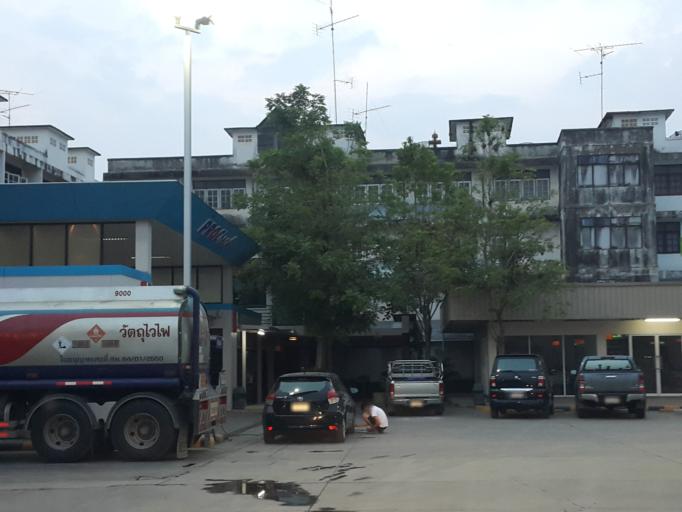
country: TH
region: Suphan Buri
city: Dan Chang
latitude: 14.8410
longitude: 99.6895
